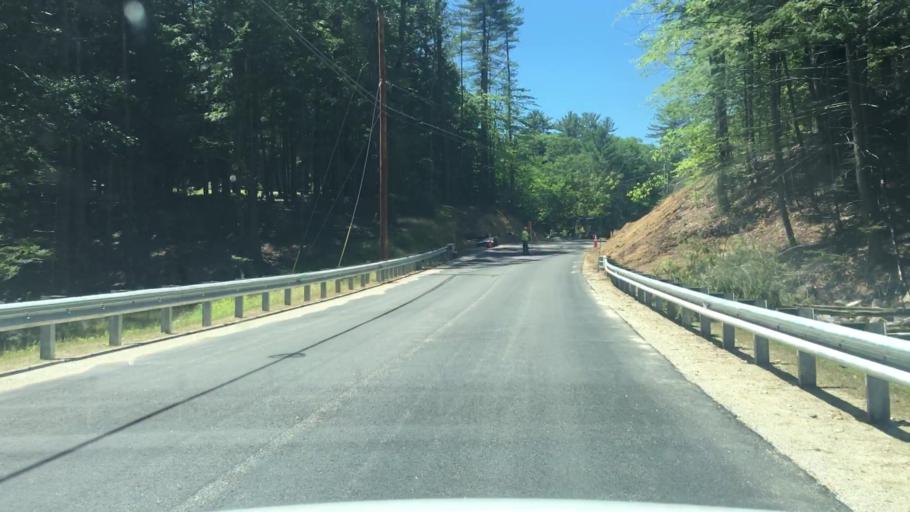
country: US
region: New Hampshire
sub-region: Merrimack County
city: Hopkinton
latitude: 43.2009
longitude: -71.6692
